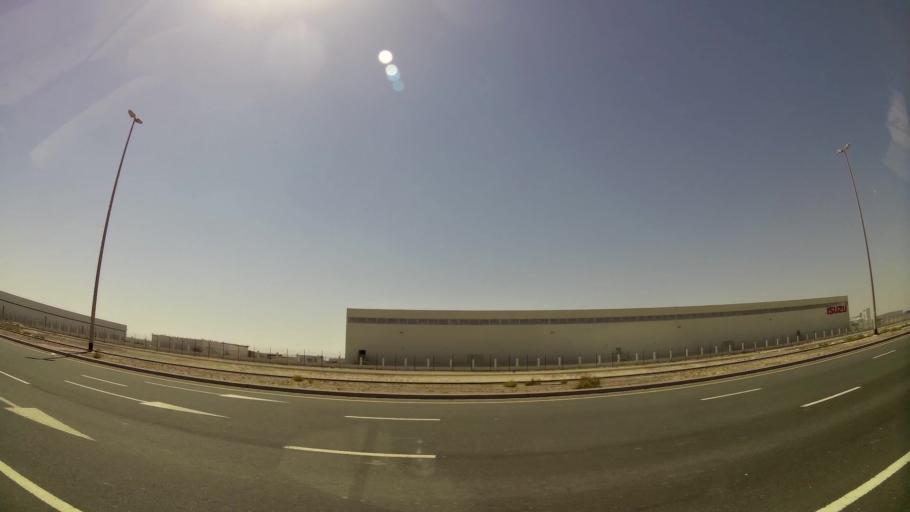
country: AE
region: Dubai
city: Dubai
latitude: 24.9617
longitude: 55.1225
